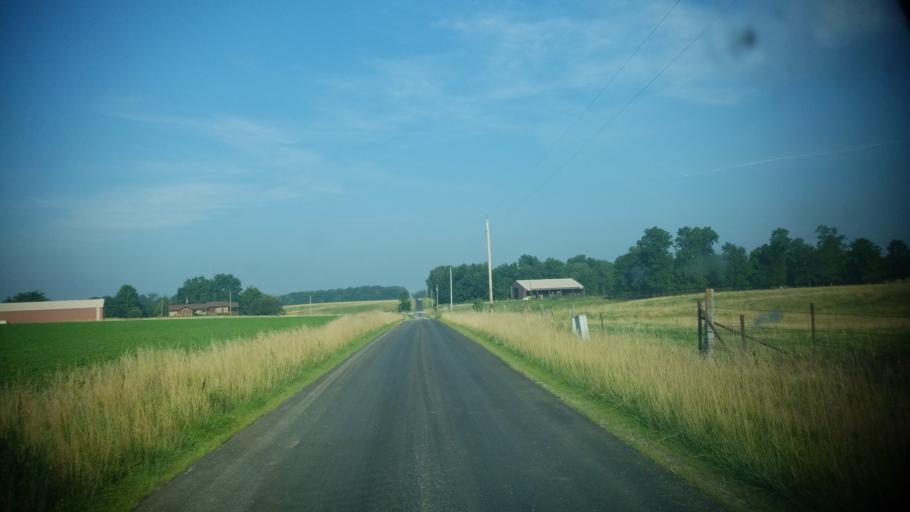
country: US
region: Illinois
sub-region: Clay County
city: Flora
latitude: 38.6025
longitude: -88.3853
